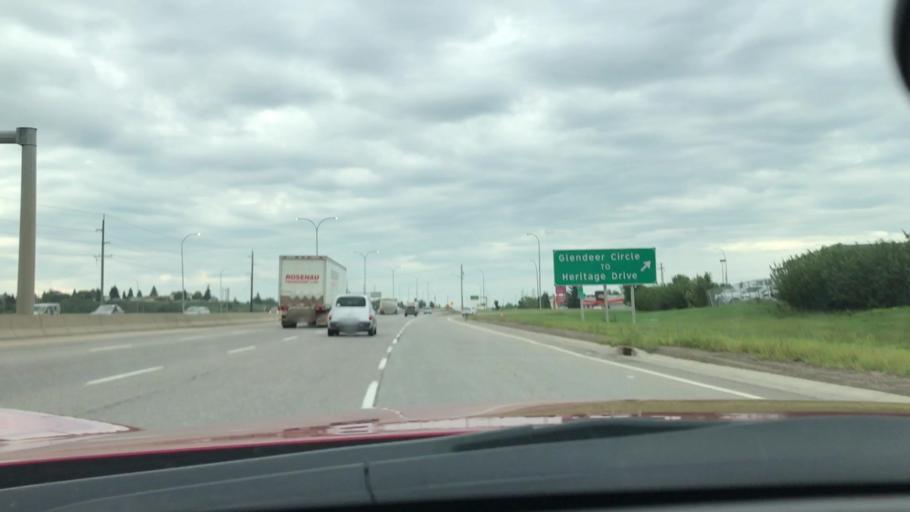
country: CA
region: Alberta
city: Calgary
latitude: 50.9906
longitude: -114.0299
